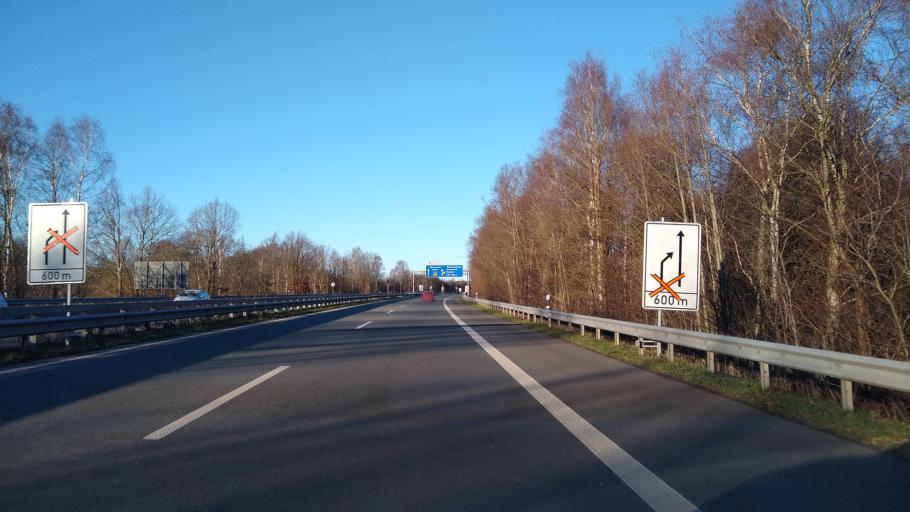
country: DE
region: Lower Saxony
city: Rastede
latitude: 53.1986
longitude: 8.2214
